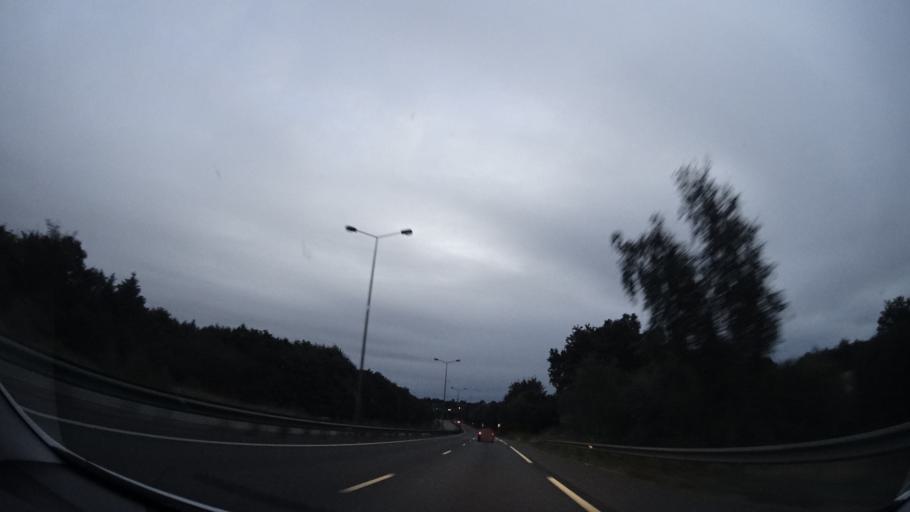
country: FR
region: Pays de la Loire
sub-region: Departement de la Mayenne
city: Laval
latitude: 48.0915
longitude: -0.7679
